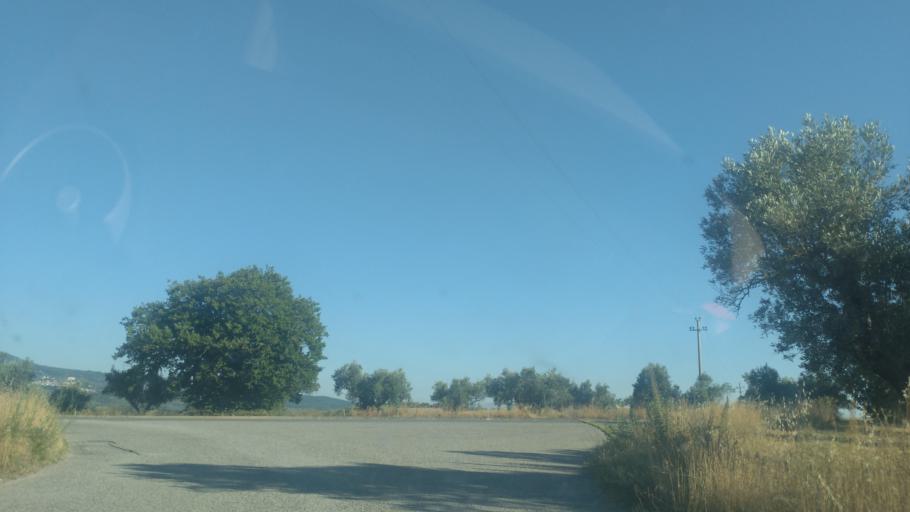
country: IT
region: Calabria
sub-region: Provincia di Catanzaro
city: Squillace
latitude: 38.7754
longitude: 16.4966
